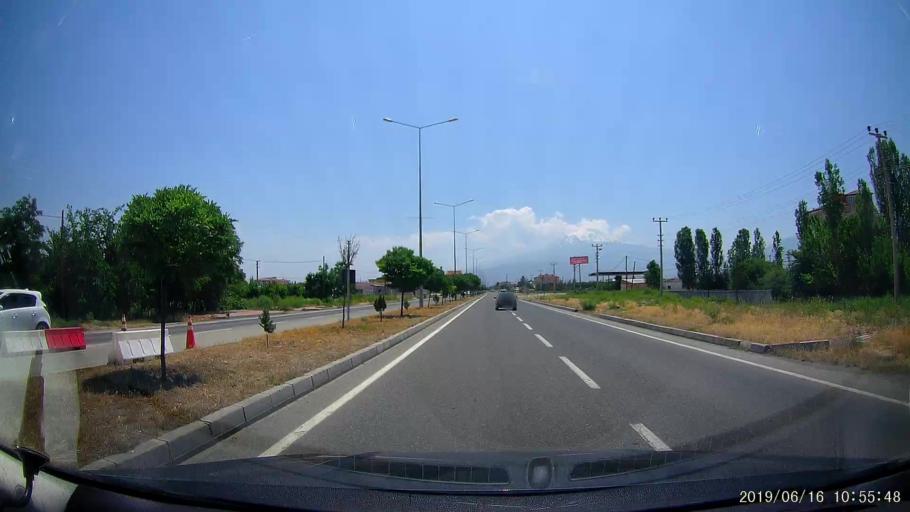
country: TR
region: Igdir
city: Igdir
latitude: 39.9342
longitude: 44.0144
